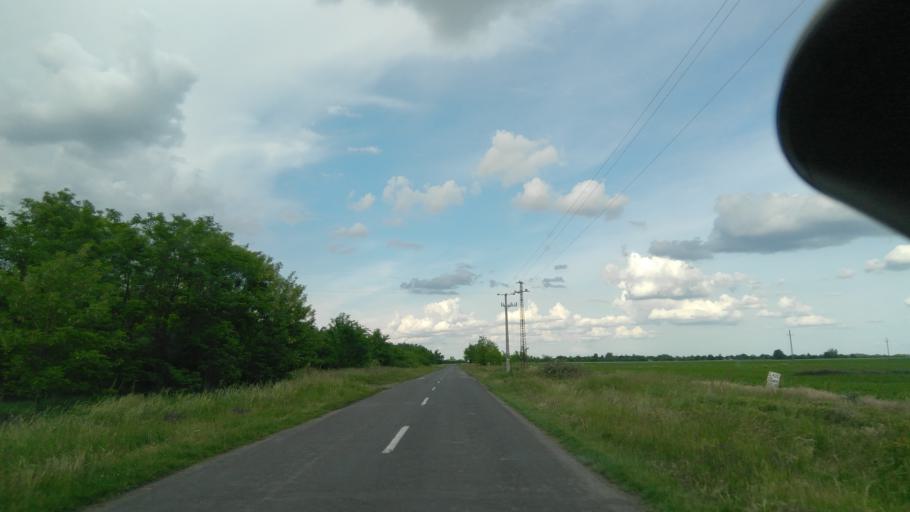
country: HU
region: Bekes
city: Dombegyhaz
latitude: 46.3332
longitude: 21.1078
